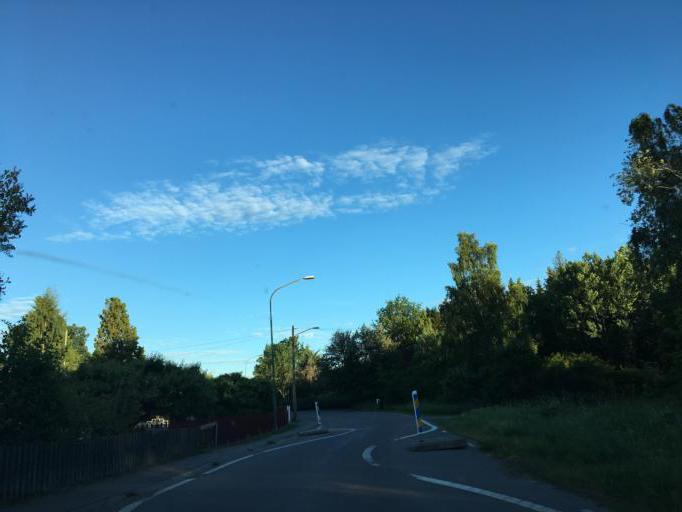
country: SE
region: Vaestmanland
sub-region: Vasteras
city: Vasteras
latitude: 59.5511
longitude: 16.5006
